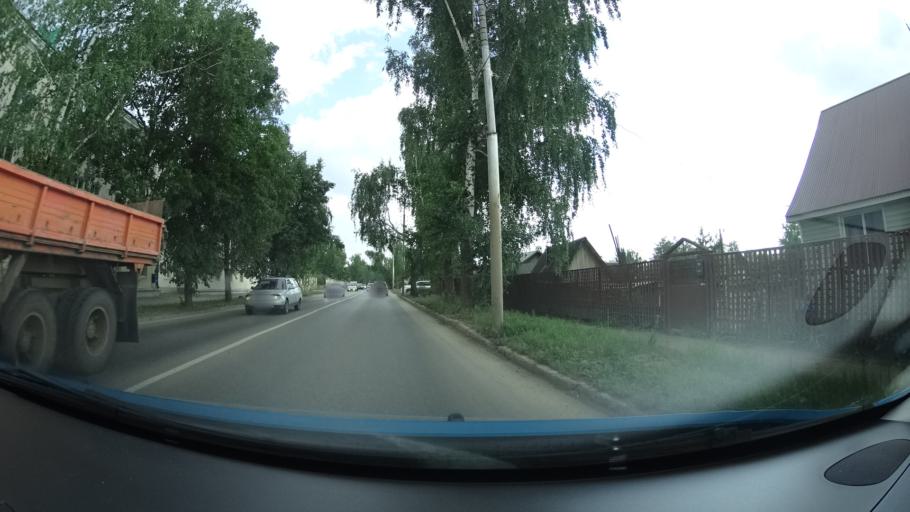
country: RU
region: Bashkortostan
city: Oktyabr'skiy
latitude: 54.4889
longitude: 53.4452
